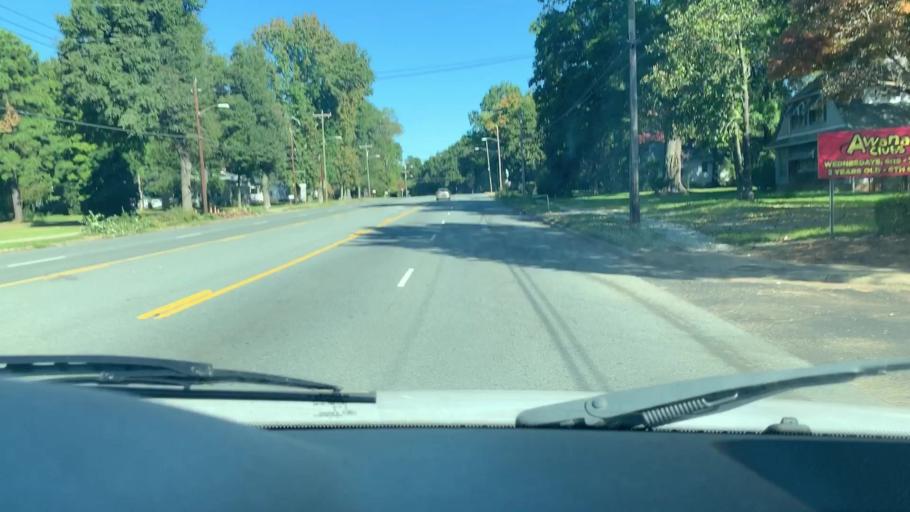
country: US
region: North Carolina
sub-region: Mecklenburg County
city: Charlotte
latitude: 35.2822
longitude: -80.7935
